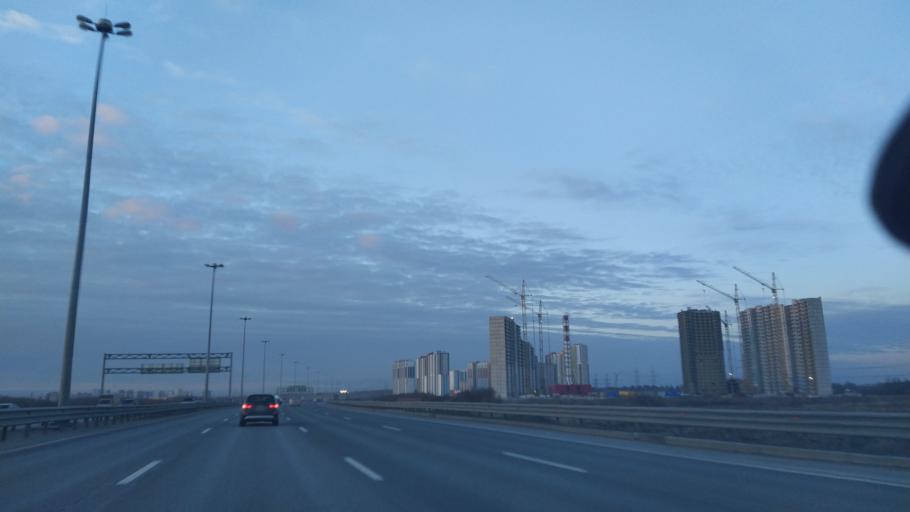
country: RU
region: St.-Petersburg
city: Krasnogvargeisky
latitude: 59.9985
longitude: 30.4769
